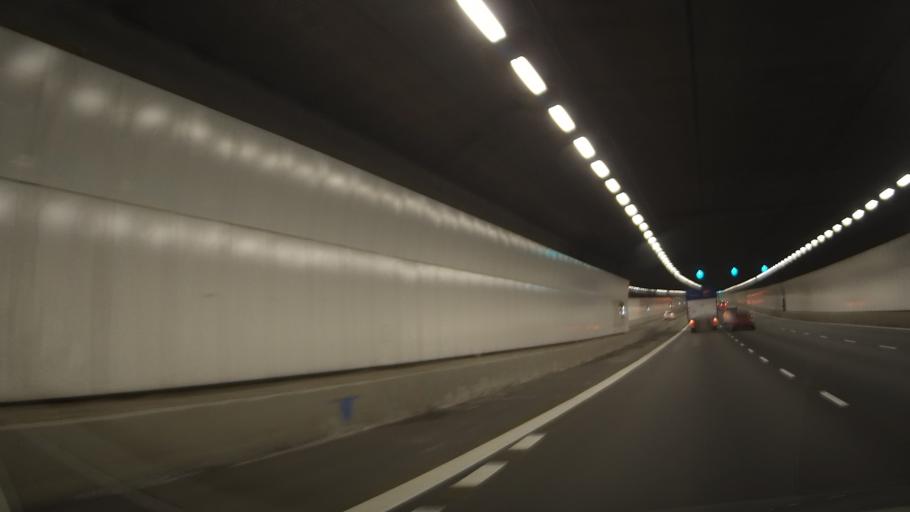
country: SG
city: Singapore
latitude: 1.2989
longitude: 103.8758
